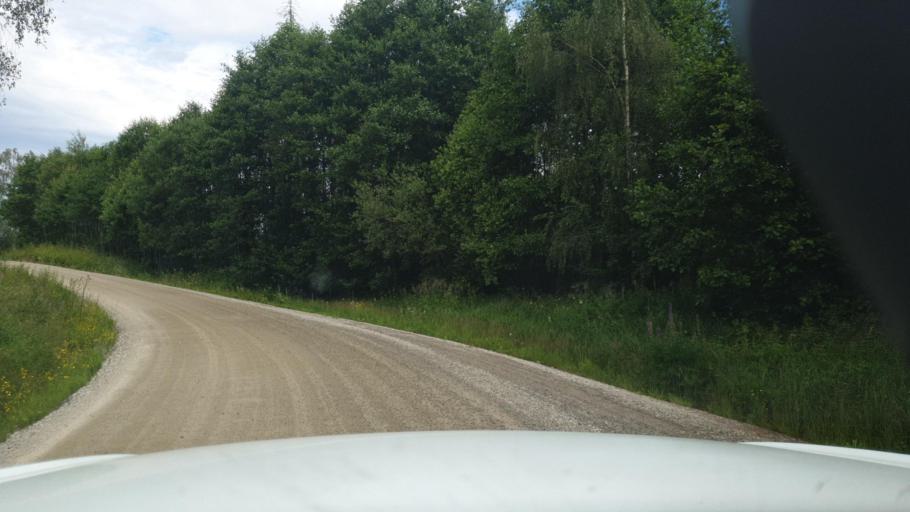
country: SE
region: Vaermland
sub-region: Arvika Kommun
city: Arvika
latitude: 59.7096
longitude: 12.8533
